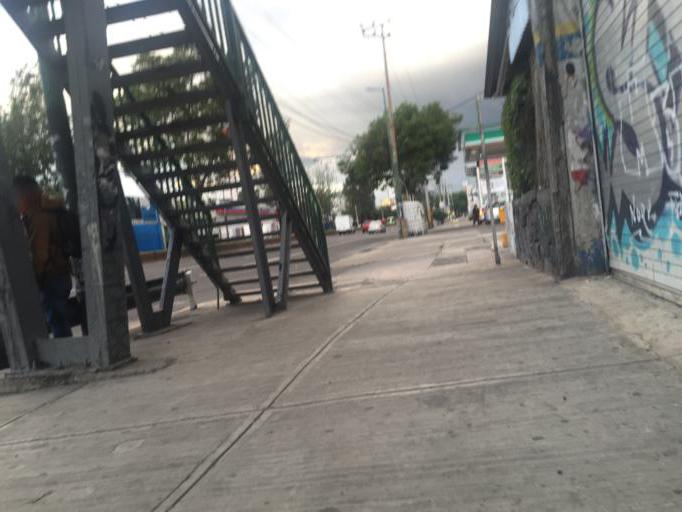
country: MX
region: Mexico City
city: Iztapalapa
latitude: 19.3545
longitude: -99.0830
